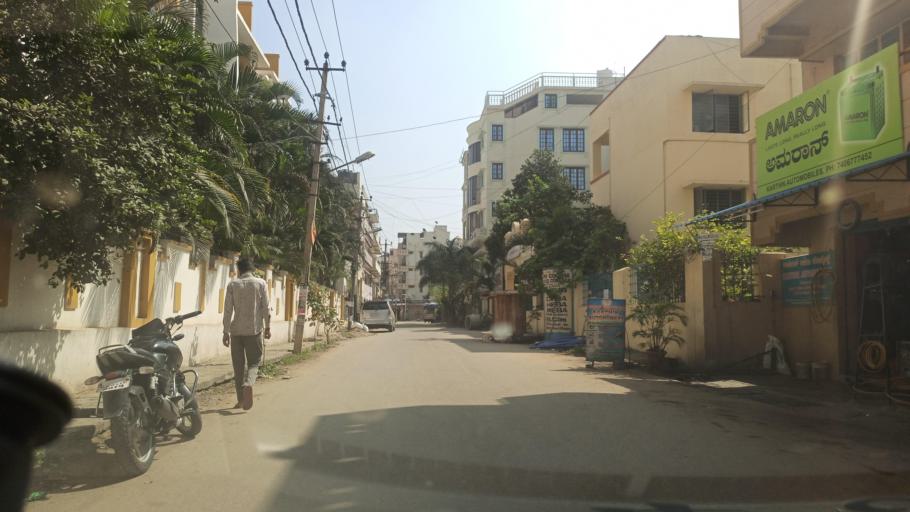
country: IN
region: Karnataka
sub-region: Bangalore Urban
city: Bangalore
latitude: 12.9526
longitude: 77.6972
